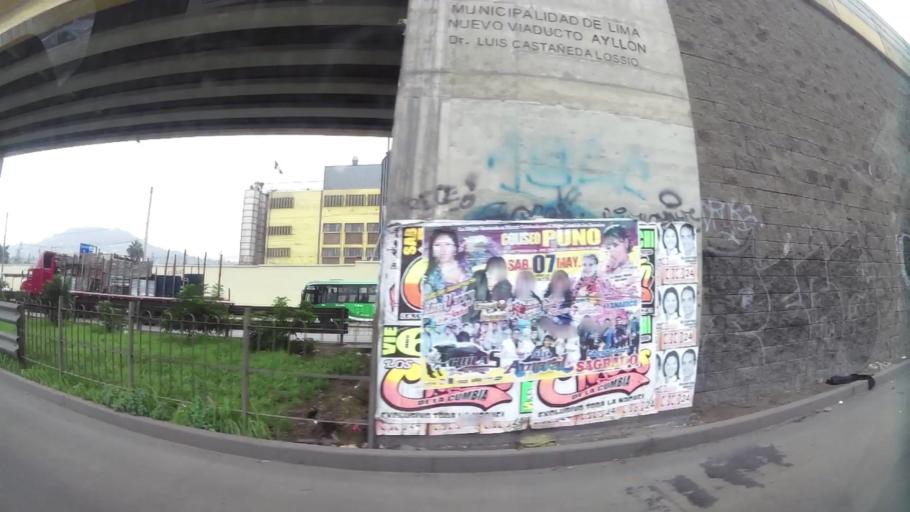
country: PE
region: Lima
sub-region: Lima
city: San Luis
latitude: -12.0642
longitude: -76.9886
